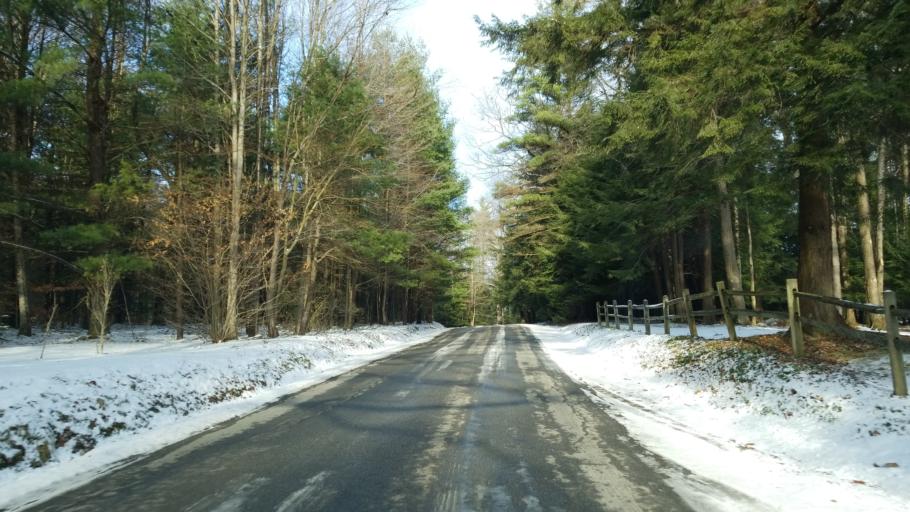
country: US
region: Pennsylvania
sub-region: Clearfield County
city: Treasure Lake
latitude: 41.0874
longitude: -78.6385
